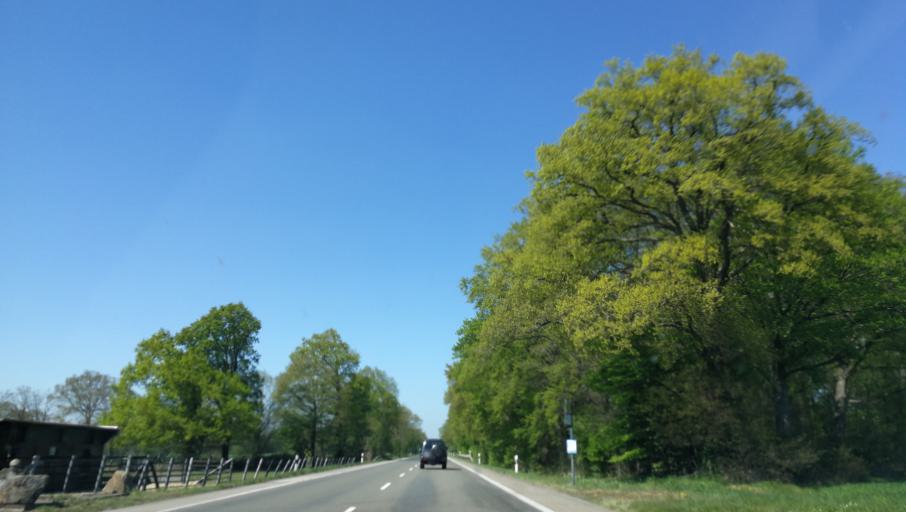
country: DE
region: North Rhine-Westphalia
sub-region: Regierungsbezirk Munster
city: Wettringen
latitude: 52.1890
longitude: 7.3290
